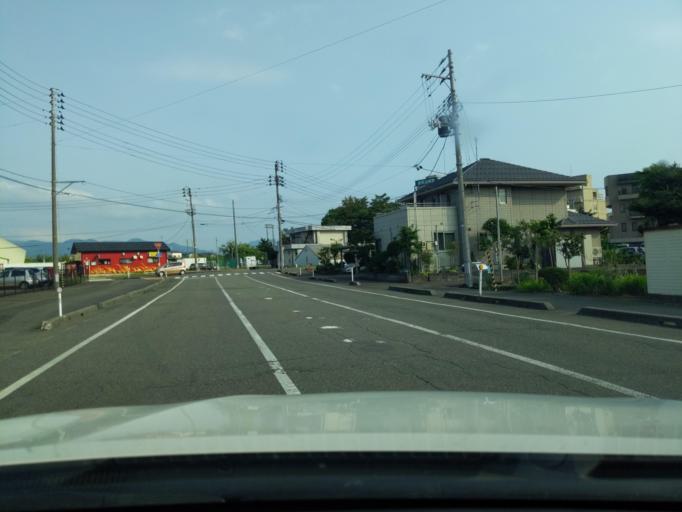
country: JP
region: Niigata
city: Nagaoka
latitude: 37.4518
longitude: 138.8158
